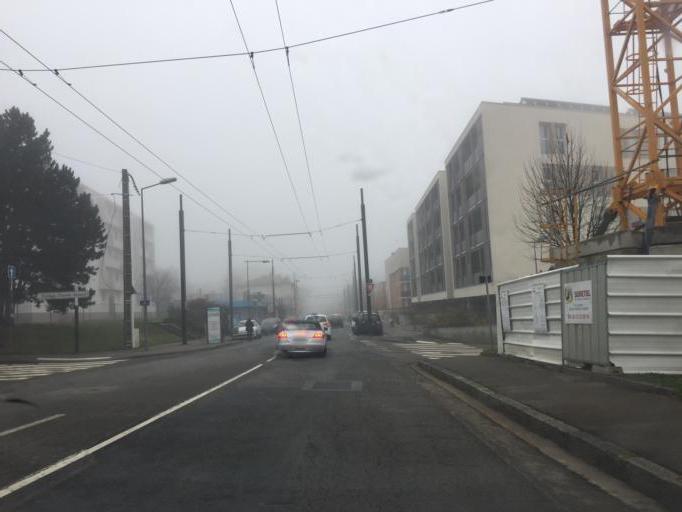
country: FR
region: Rhone-Alpes
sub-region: Departement du Rhone
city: Caluire-et-Cuire
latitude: 45.7910
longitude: 4.8427
